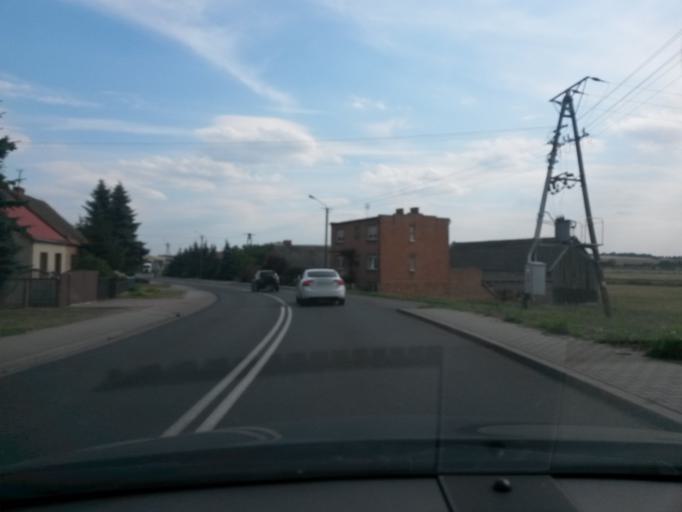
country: PL
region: Greater Poland Voivodeship
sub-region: Powiat gostynski
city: Gostyn
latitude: 51.9318
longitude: 17.0151
